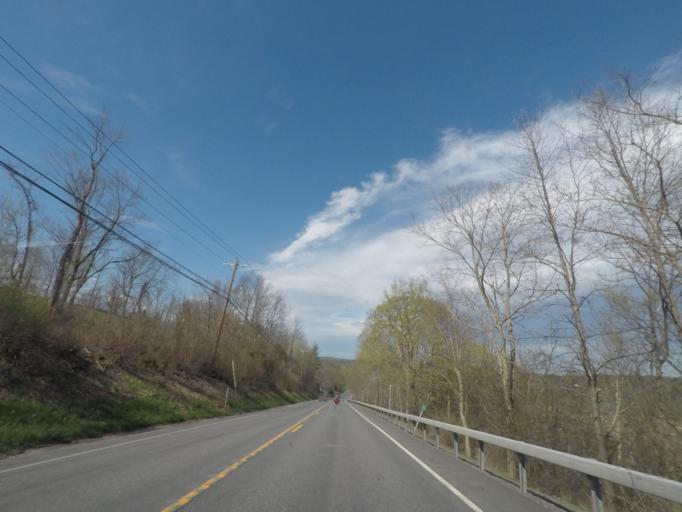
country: US
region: New York
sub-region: Greene County
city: Cairo
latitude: 42.4062
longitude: -74.0257
